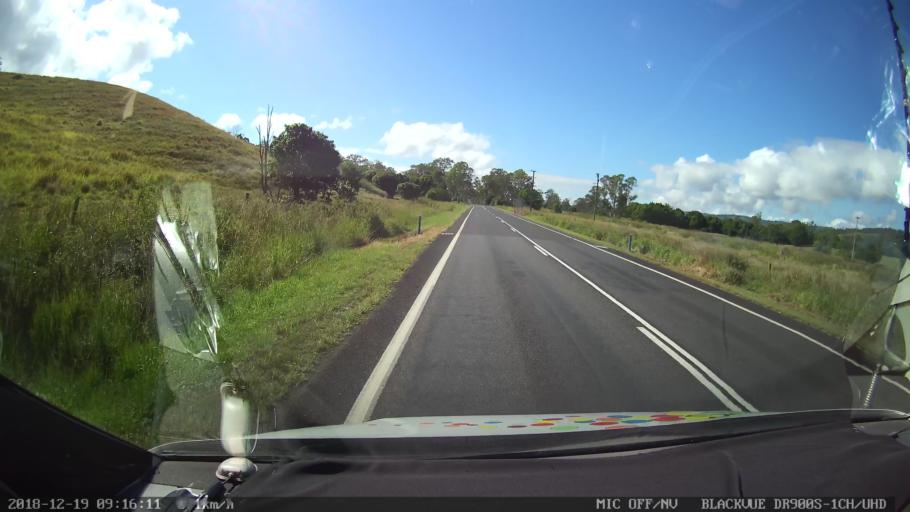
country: AU
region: New South Wales
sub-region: Kyogle
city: Kyogle
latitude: -28.5185
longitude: 152.9658
